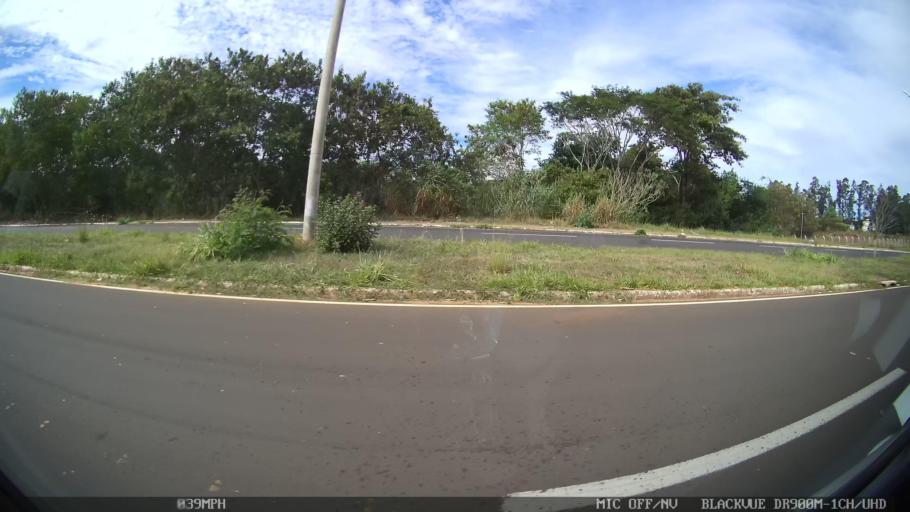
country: BR
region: Sao Paulo
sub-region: Catanduva
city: Catanduva
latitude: -21.1515
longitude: -48.9521
